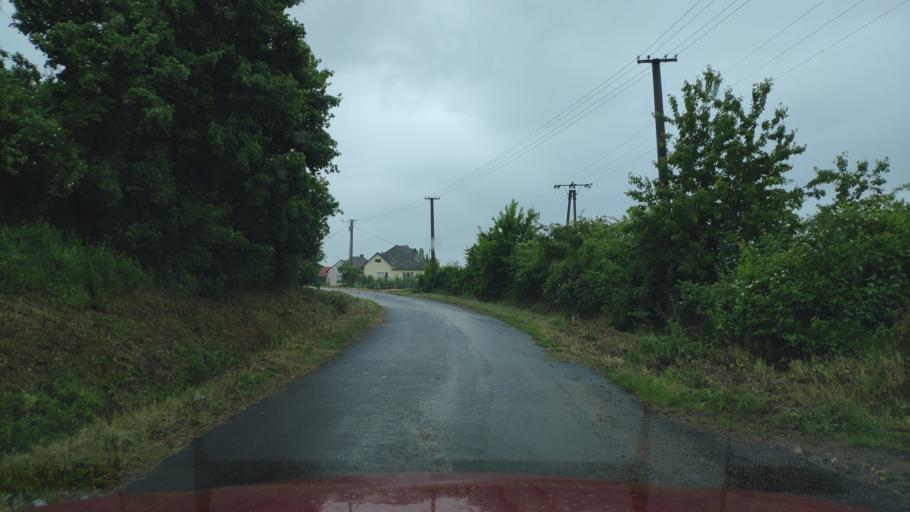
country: HU
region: Borsod-Abauj-Zemplen
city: Satoraljaujhely
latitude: 48.4210
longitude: 21.7112
